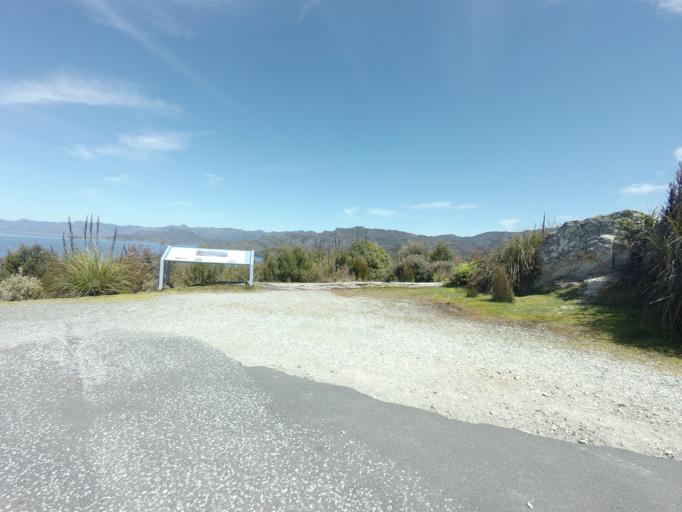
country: AU
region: Tasmania
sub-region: West Coast
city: Queenstown
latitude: -42.7834
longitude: 146.0323
